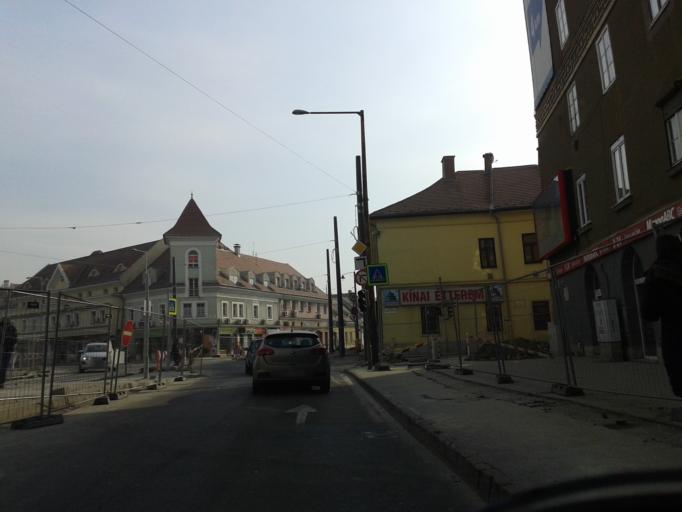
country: HU
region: Budapest
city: Budapest III. keruelet
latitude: 47.5325
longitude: 19.0365
